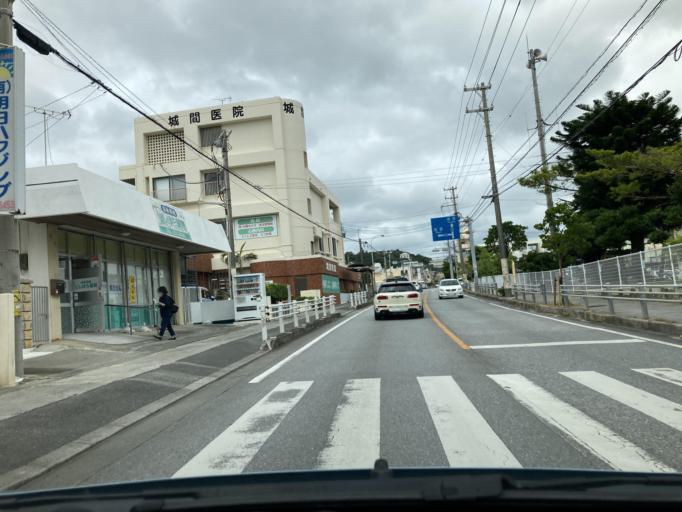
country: JP
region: Okinawa
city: Ginowan
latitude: 26.2285
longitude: 127.7543
